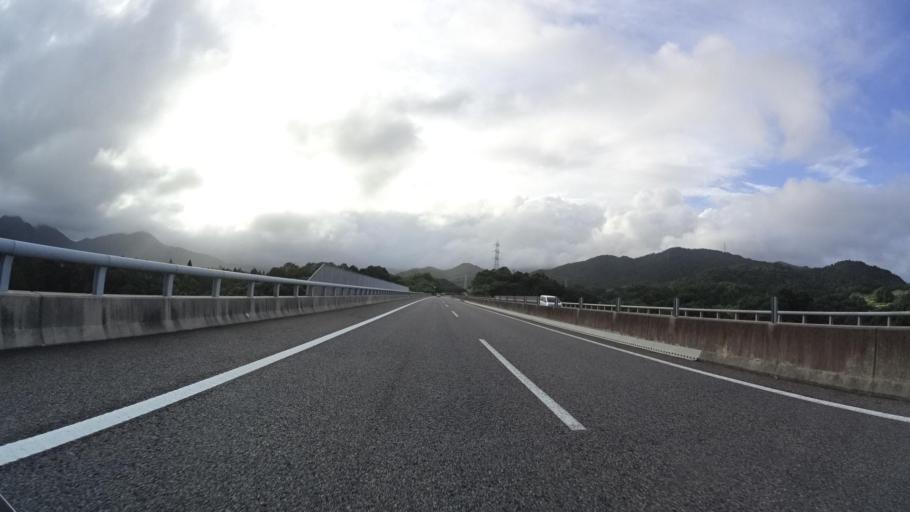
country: JP
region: Mie
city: Kameyama
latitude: 34.9050
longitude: 136.4370
